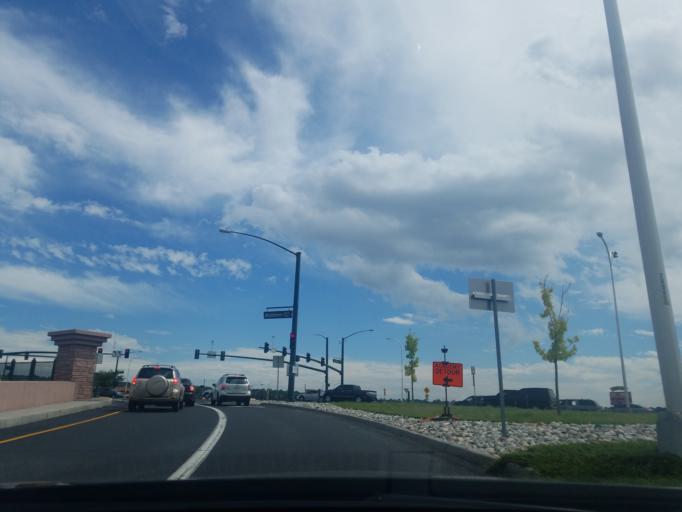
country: US
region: Colorado
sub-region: El Paso County
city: Air Force Academy
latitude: 38.9331
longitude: -104.7970
